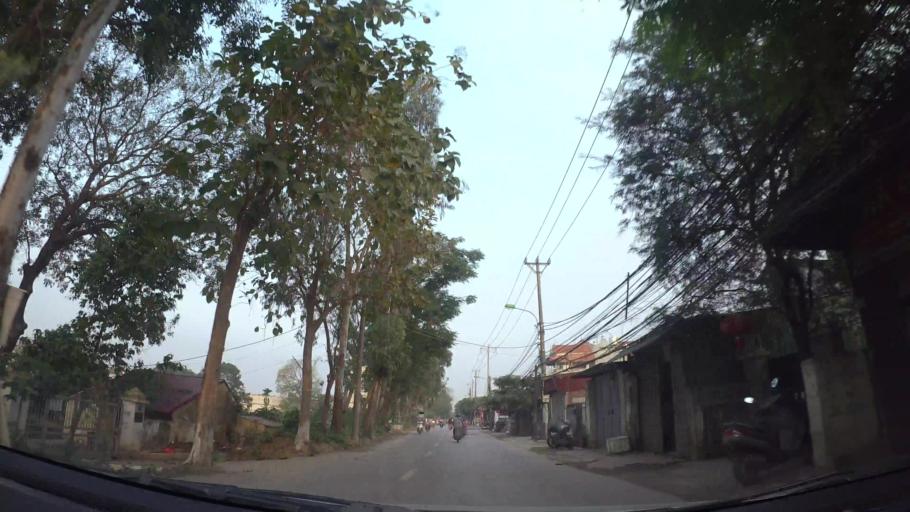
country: VN
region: Ha Noi
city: Tay Ho
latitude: 21.0750
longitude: 105.7969
